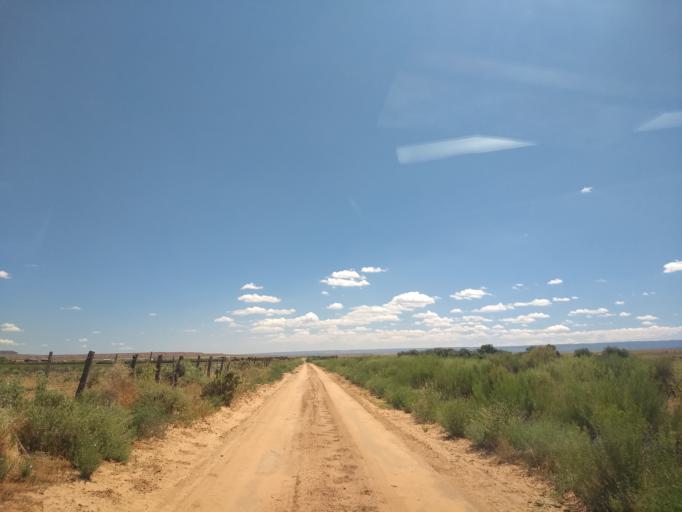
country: US
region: Arizona
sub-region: Coconino County
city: Fredonia
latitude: 36.9251
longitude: -112.5434
